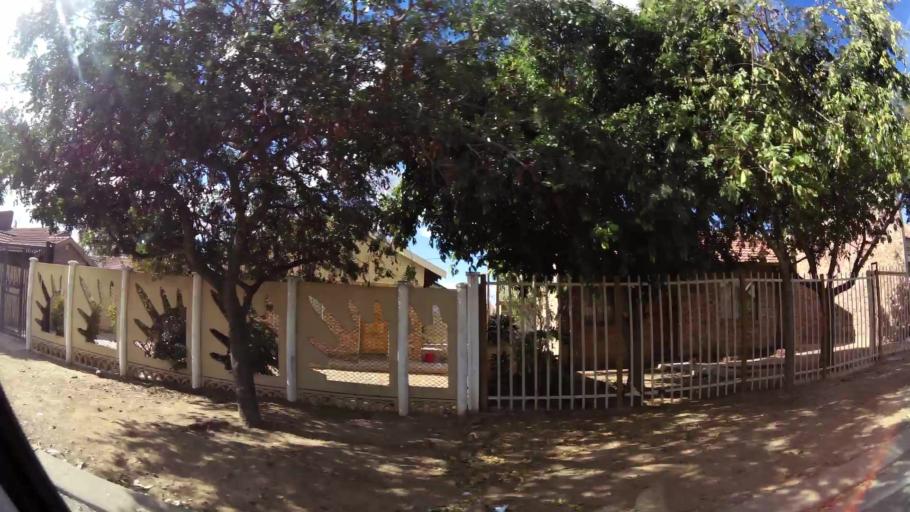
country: ZA
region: Limpopo
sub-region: Capricorn District Municipality
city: Polokwane
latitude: -23.8853
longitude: 29.4716
